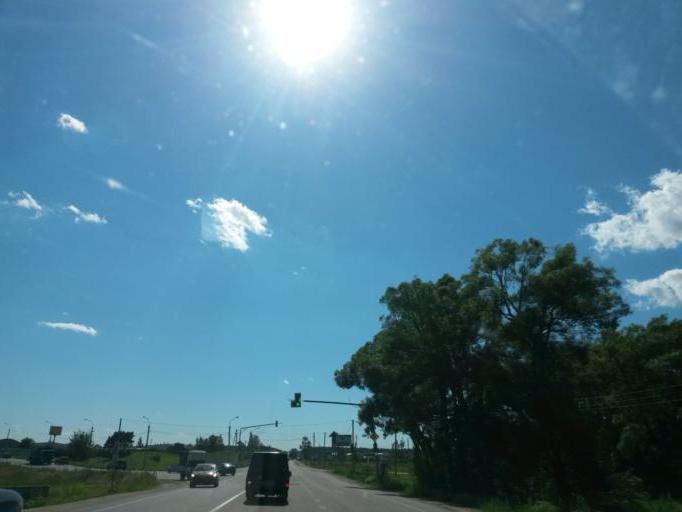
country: RU
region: Moskovskaya
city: Protvino
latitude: 54.8908
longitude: 37.2957
